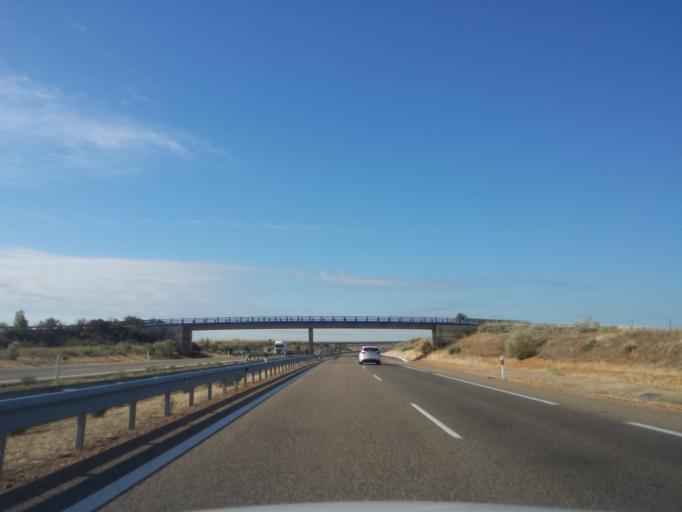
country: ES
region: Castille and Leon
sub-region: Provincia de Leon
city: Villamanan
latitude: 42.3645
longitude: -5.5957
